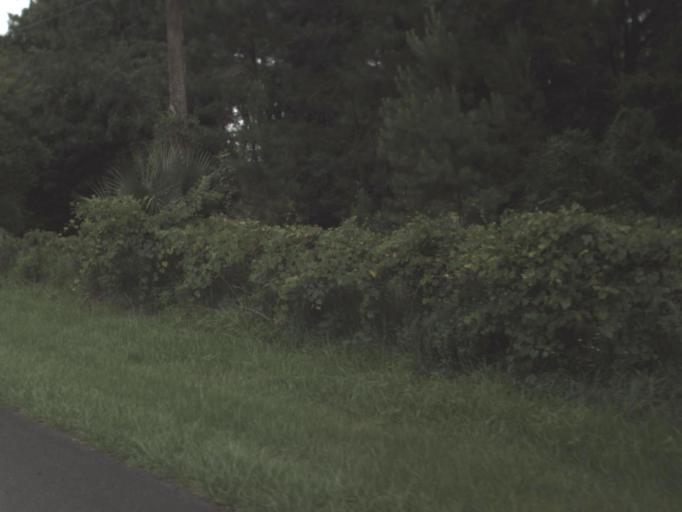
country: US
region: Florida
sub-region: Alachua County
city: Archer
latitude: 29.5210
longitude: -82.5184
